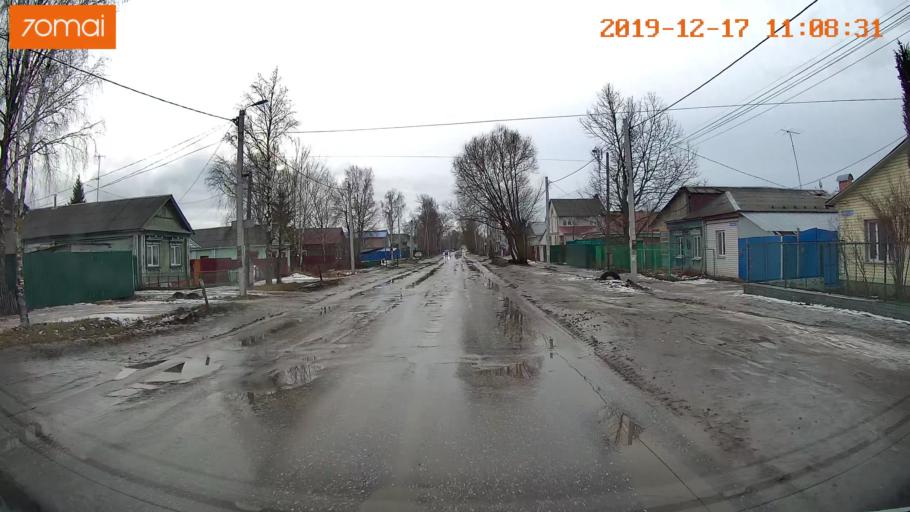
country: RU
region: Vladimir
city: Gus'-Khrustal'nyy
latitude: 55.6071
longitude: 40.6432
